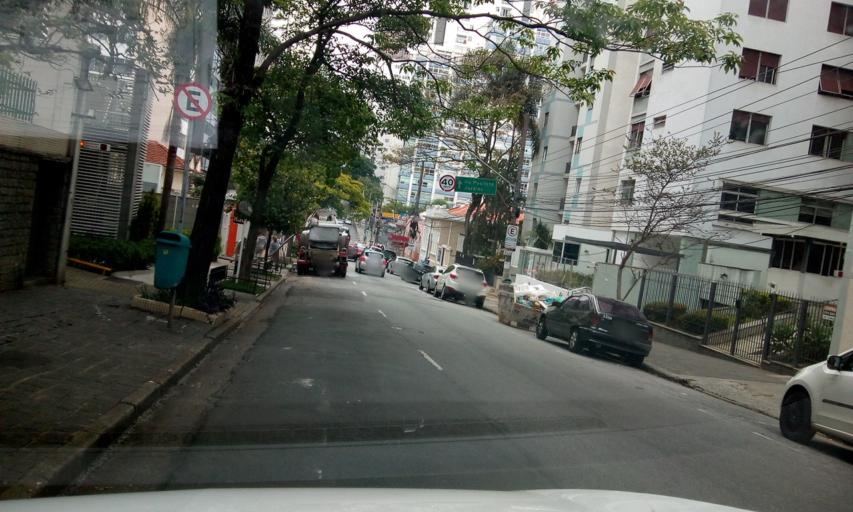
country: BR
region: Sao Paulo
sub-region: Sao Paulo
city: Sao Paulo
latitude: -23.5634
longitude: -46.6482
